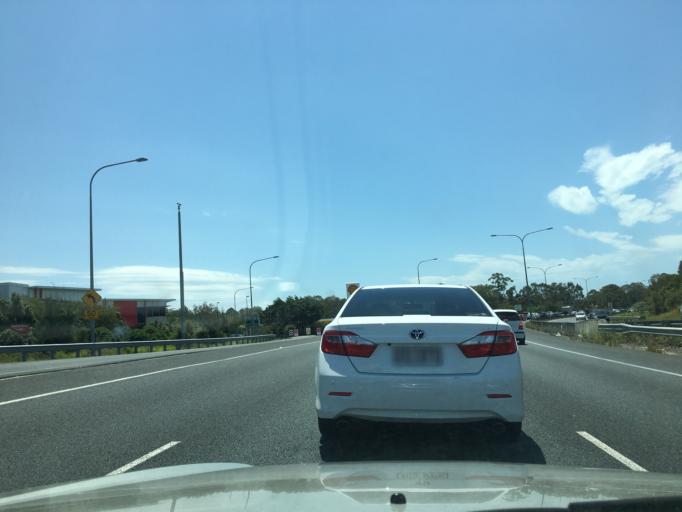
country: AU
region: Queensland
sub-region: Brisbane
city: Wavell Heights
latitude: -27.3799
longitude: 153.0938
